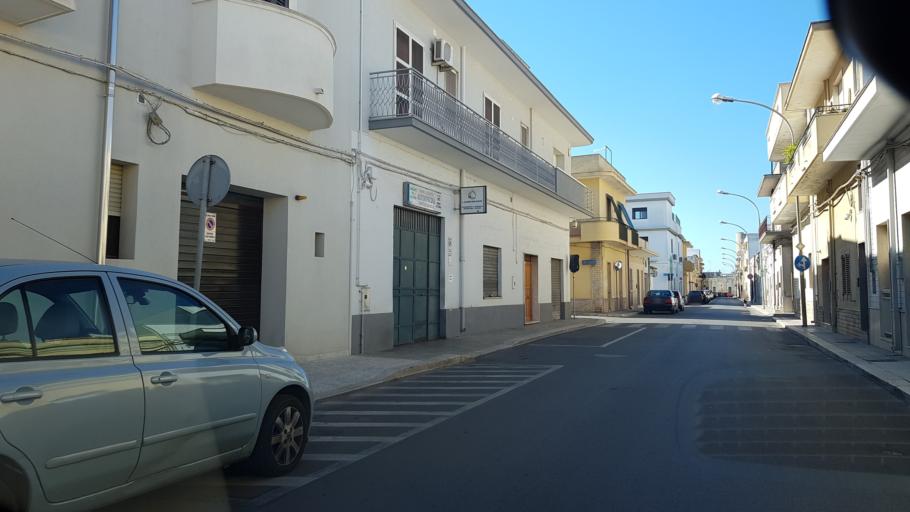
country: IT
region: Apulia
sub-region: Provincia di Brindisi
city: Mesagne
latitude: 40.5537
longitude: 17.8101
